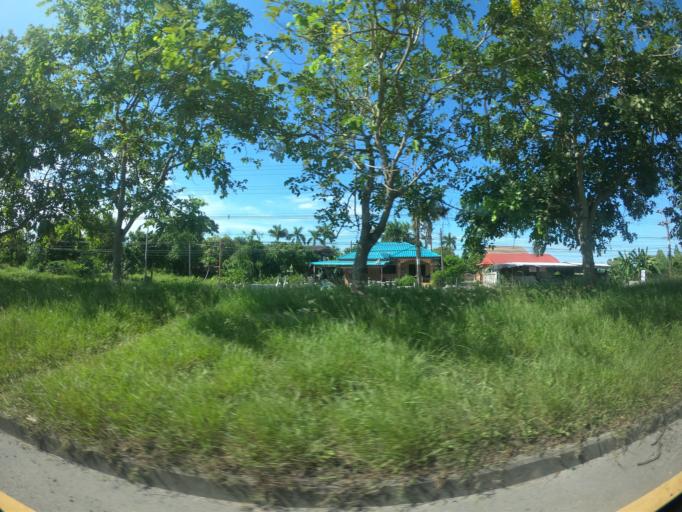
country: TH
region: Nakhon Nayok
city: Ban Na
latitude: 14.2398
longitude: 101.1311
